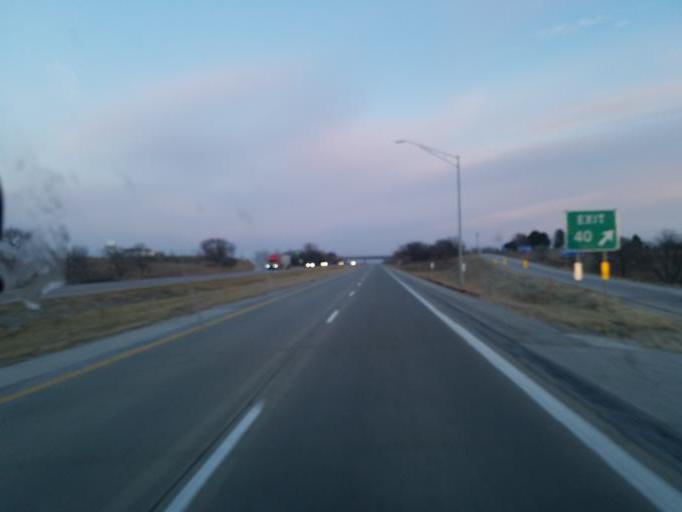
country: US
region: Iowa
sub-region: Pottawattamie County
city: Avoca
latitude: 41.4976
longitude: -95.3435
